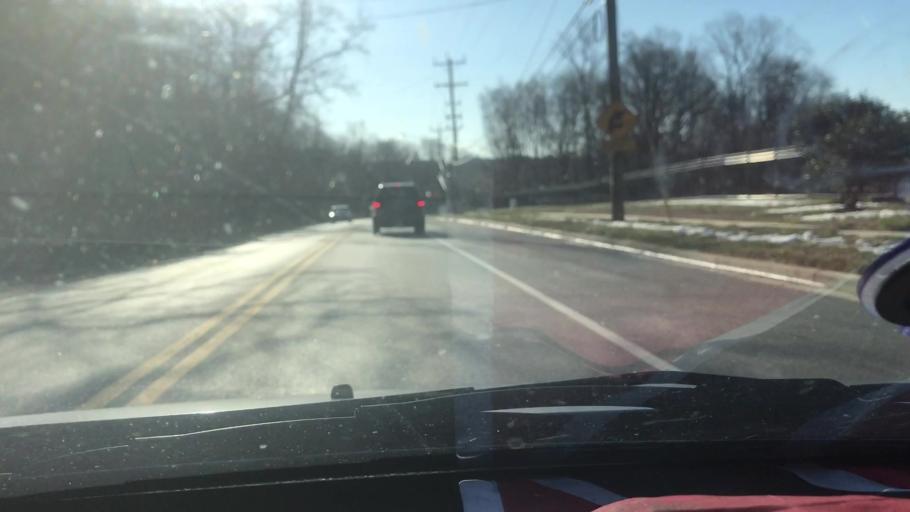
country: US
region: Maryland
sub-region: Prince George's County
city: Suitland
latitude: 38.8449
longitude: -76.9185
